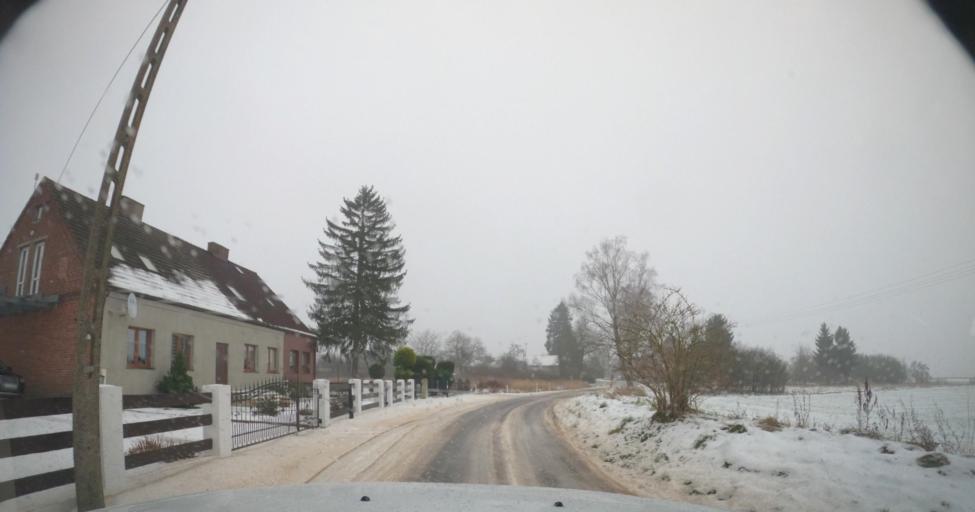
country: PL
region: West Pomeranian Voivodeship
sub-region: Powiat kamienski
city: Golczewo
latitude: 53.8686
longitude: 15.0689
